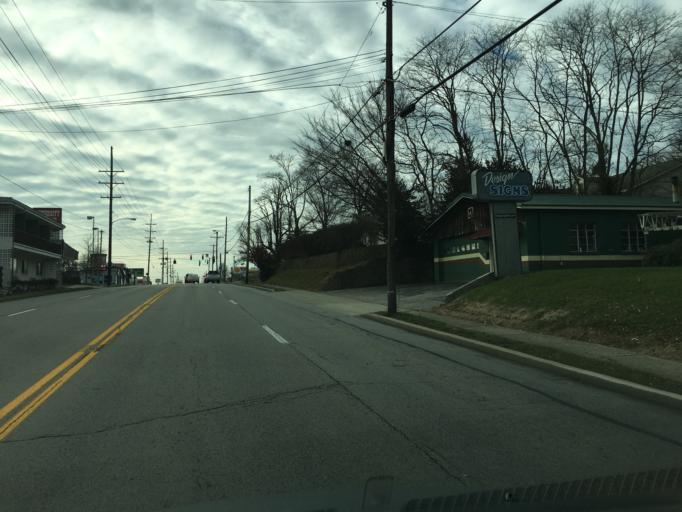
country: US
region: Kentucky
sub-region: Franklin County
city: Frankfort
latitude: 38.2040
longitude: -84.8446
